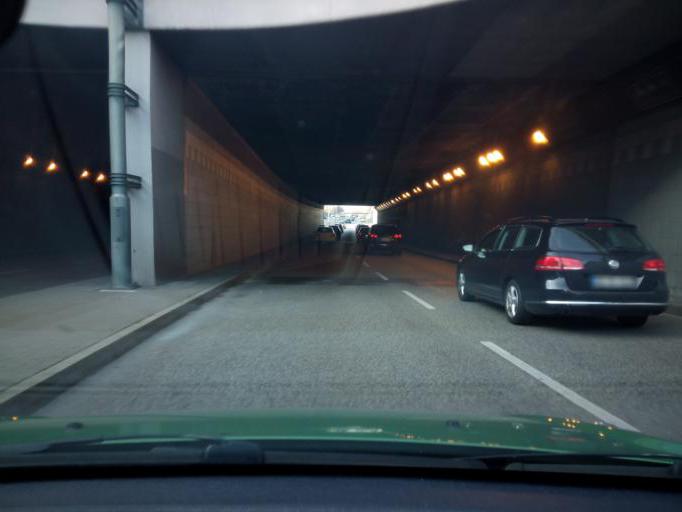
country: DE
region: Berlin
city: Friedrichsfelde
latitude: 52.5096
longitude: 13.5198
